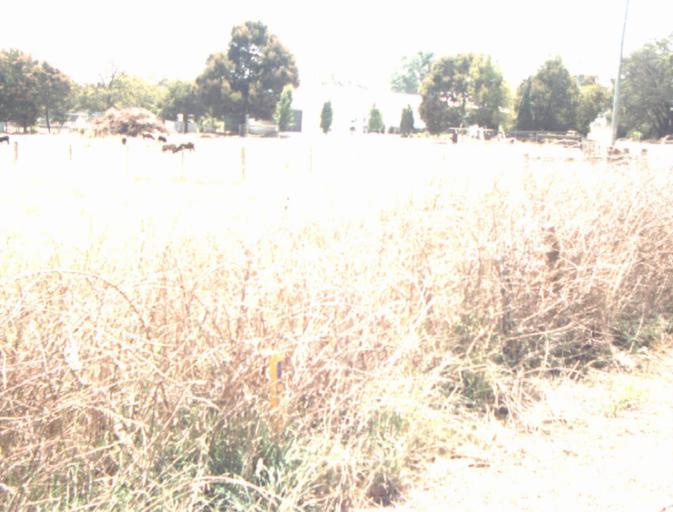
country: AU
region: Tasmania
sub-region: Northern Midlands
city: Perth
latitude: -41.5034
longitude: 147.2054
